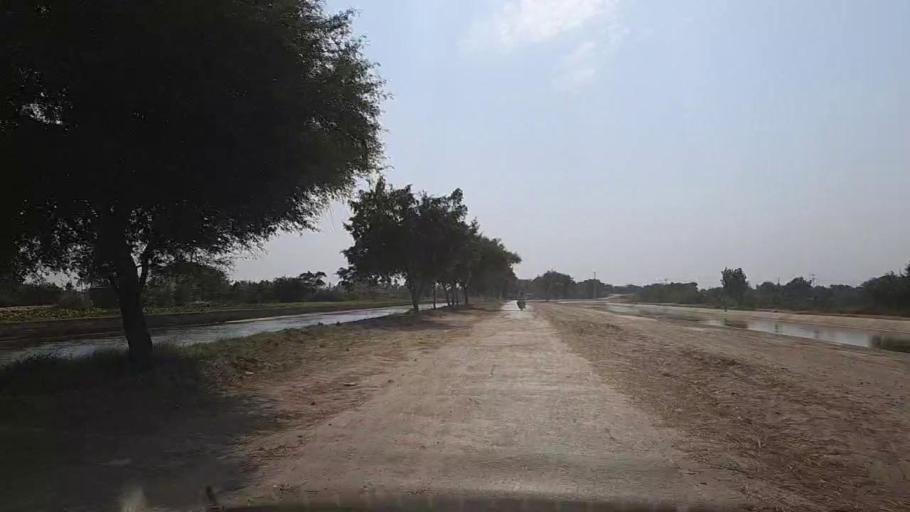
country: PK
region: Sindh
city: Thatta
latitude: 24.7429
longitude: 67.7652
